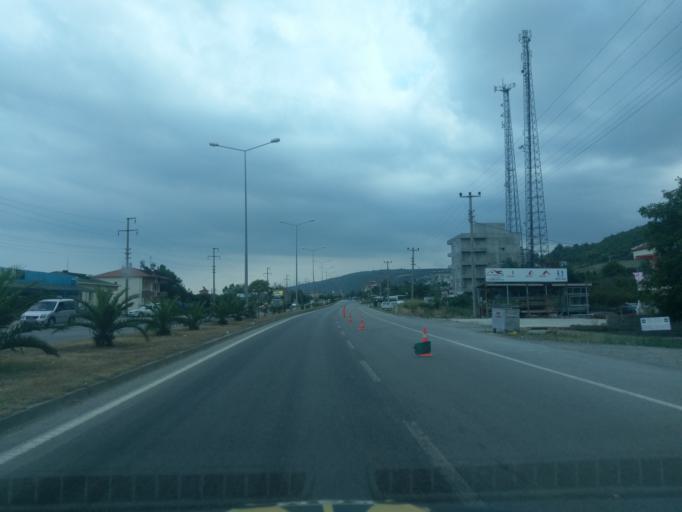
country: TR
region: Samsun
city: Taflan
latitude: 41.4141
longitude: 36.1738
